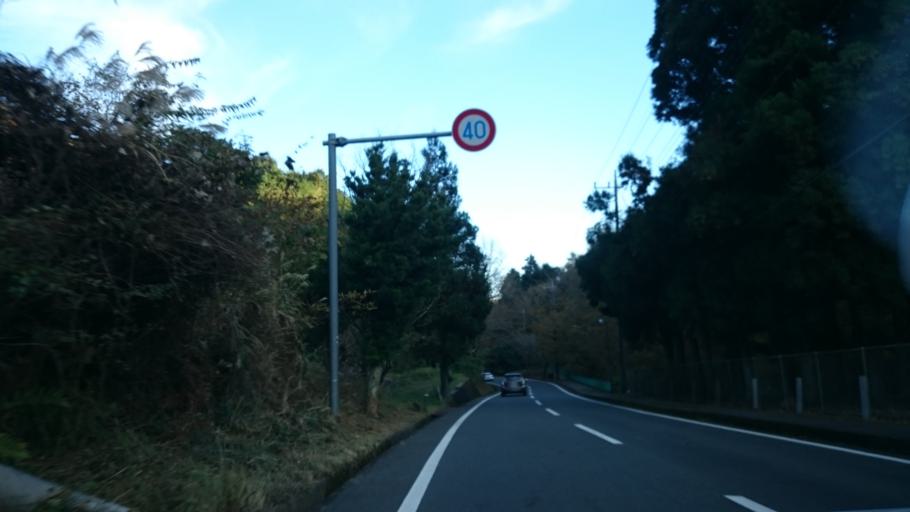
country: JP
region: Shizuoka
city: Numazu
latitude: 34.9772
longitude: 138.9229
